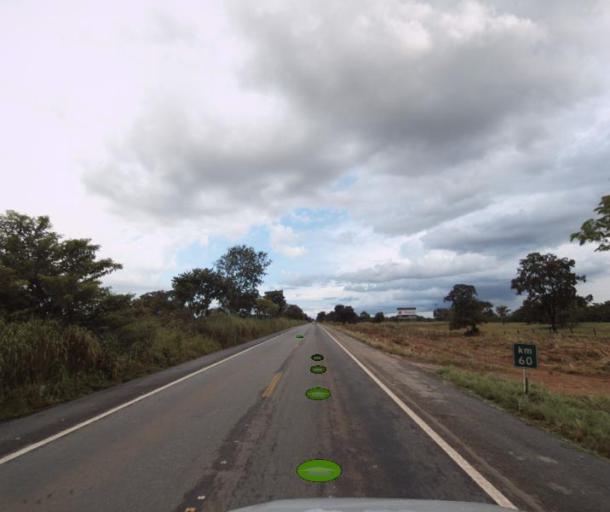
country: BR
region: Goias
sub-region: Porangatu
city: Porangatu
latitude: -13.3371
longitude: -49.1209
